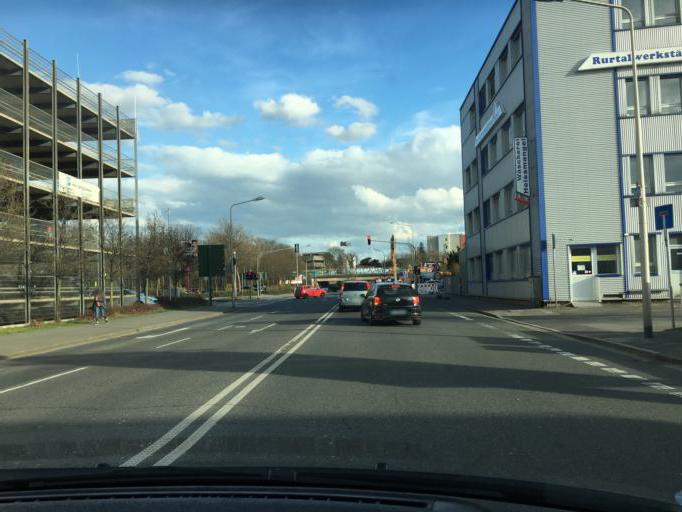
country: DE
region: North Rhine-Westphalia
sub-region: Regierungsbezirk Koln
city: Dueren
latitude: 50.8076
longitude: 6.4765
